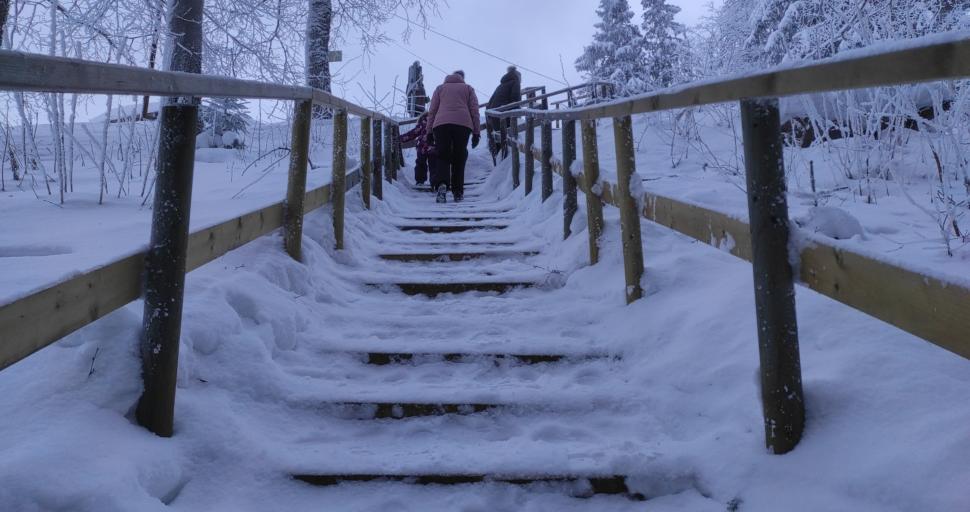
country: LV
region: Vecpiebalga
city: Vecpiebalga
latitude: 56.8747
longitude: 25.9630
